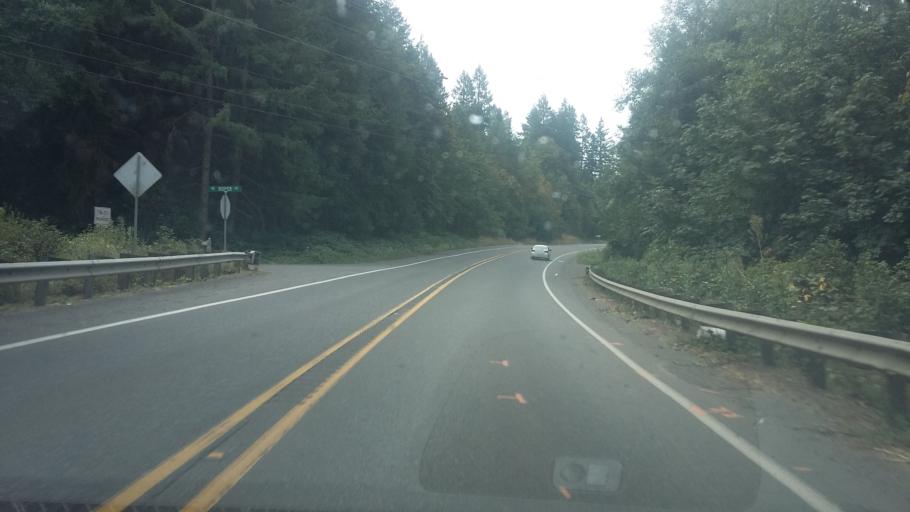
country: US
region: Washington
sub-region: Clark County
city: Lewisville
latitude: 45.8096
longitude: -122.5472
